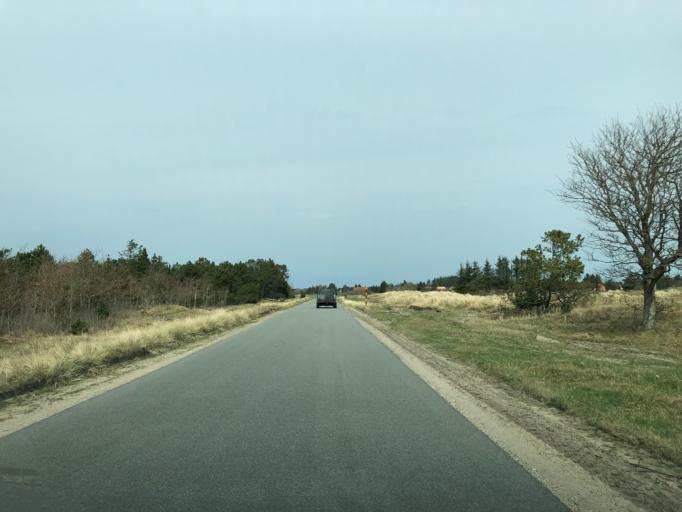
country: DK
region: South Denmark
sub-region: Varde Kommune
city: Oksbol
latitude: 55.6363
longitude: 8.1731
